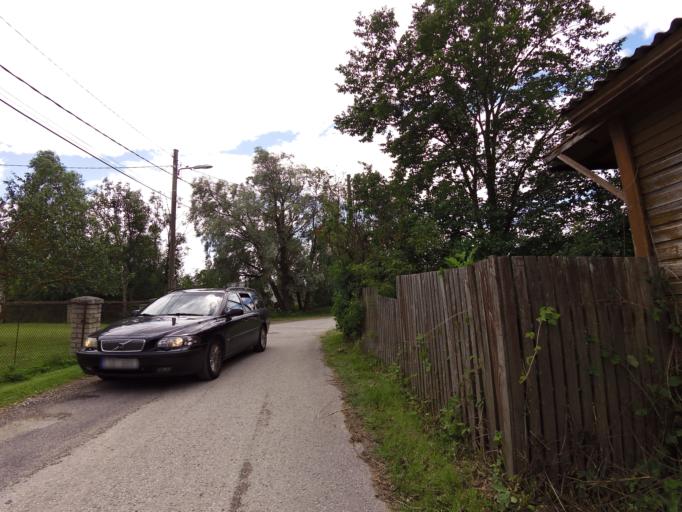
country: EE
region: Laeaene
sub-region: Haapsalu linn
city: Haapsalu
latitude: 58.9572
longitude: 23.5259
